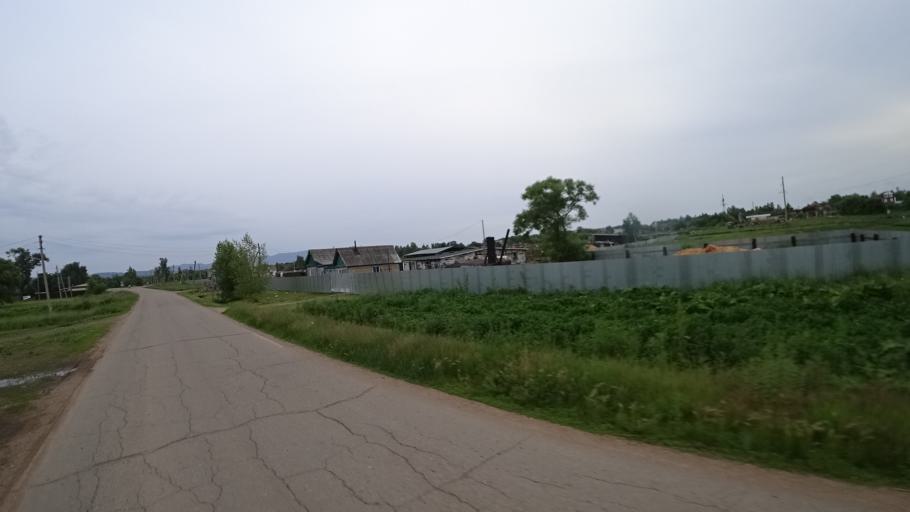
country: RU
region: Primorskiy
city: Novosysoyevka
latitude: 44.2332
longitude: 133.3708
